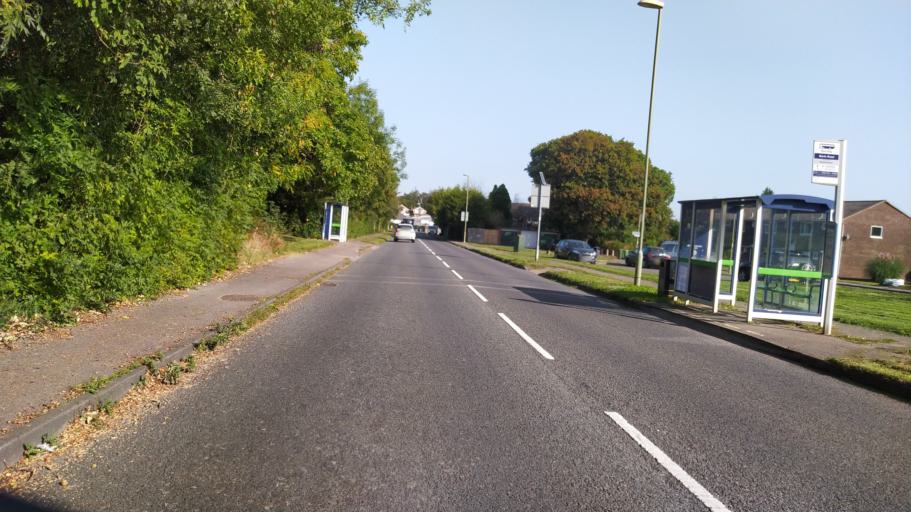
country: GB
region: England
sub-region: Hampshire
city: Hedge End
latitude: 50.9128
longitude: -1.2908
